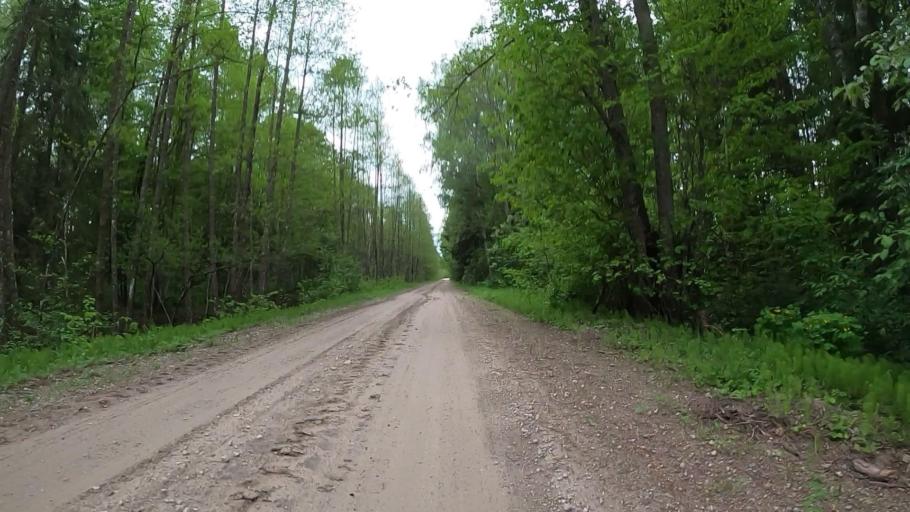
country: LV
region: Ozolnieku
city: Ozolnieki
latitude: 56.7927
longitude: 23.7770
